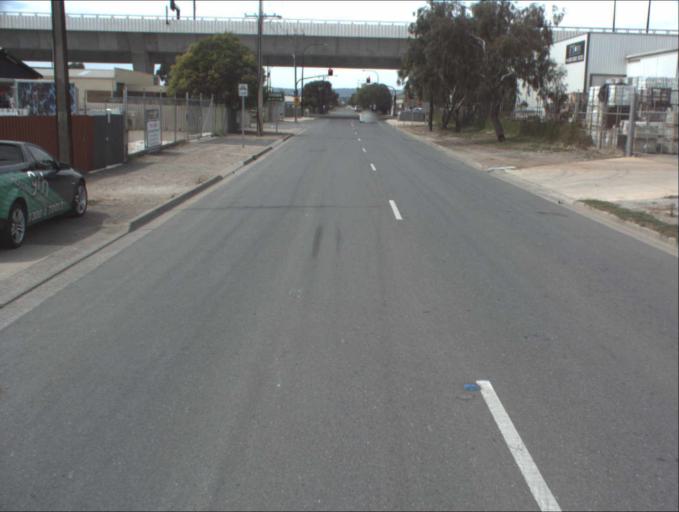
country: AU
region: South Australia
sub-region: Charles Sturt
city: Woodville North
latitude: -34.8389
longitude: 138.5620
